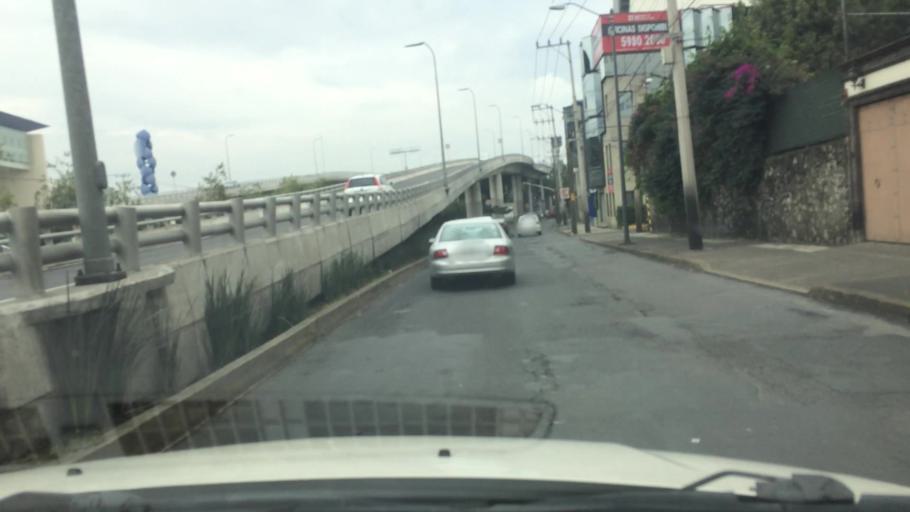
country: MX
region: Mexico City
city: Tlalpan
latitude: 19.2862
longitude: -99.1480
